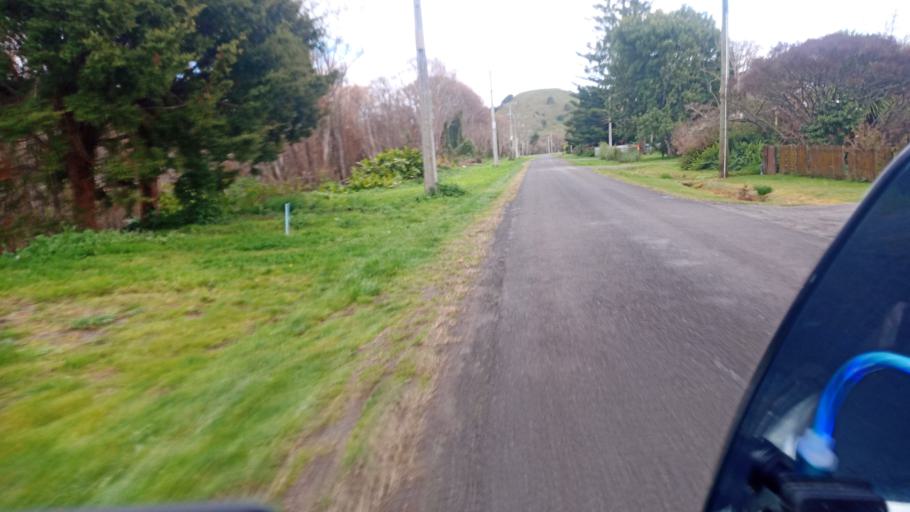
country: NZ
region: Gisborne
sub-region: Gisborne District
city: Gisborne
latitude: -38.3724
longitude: 178.2899
